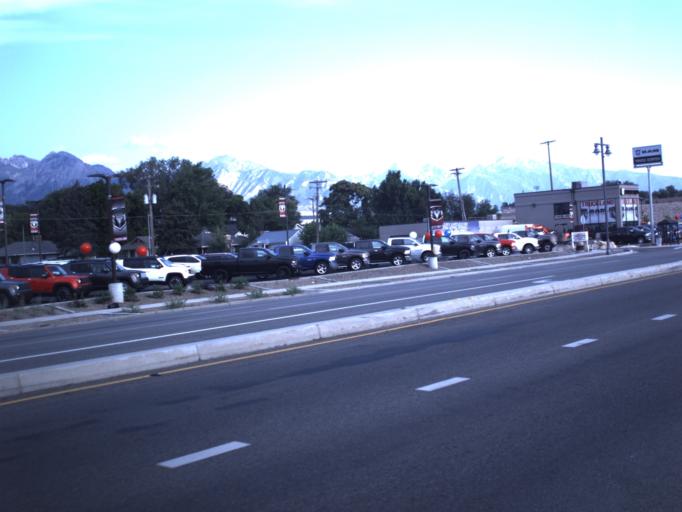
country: US
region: Utah
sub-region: Salt Lake County
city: South Salt Lake
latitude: 40.7202
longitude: -111.8884
